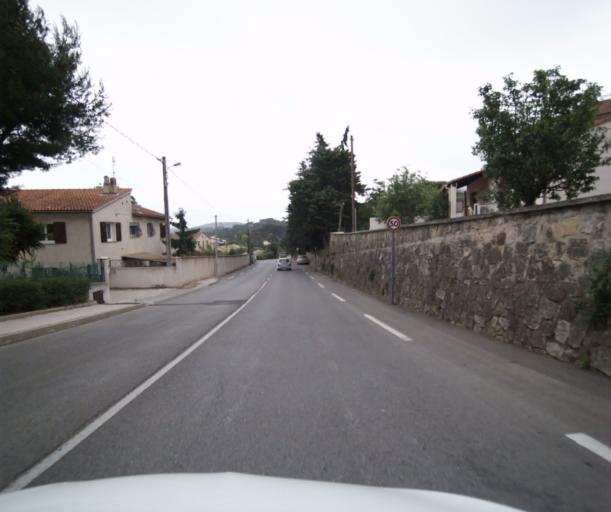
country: FR
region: Provence-Alpes-Cote d'Azur
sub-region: Departement du Var
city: La Seyne-sur-Mer
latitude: 43.0897
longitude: 5.8693
